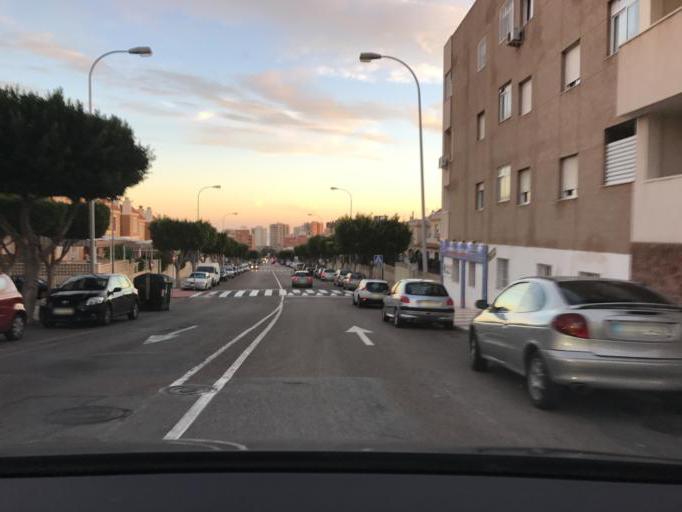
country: ES
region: Andalusia
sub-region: Provincia de Almeria
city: Aguadulce
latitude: 36.8179
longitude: -2.5814
